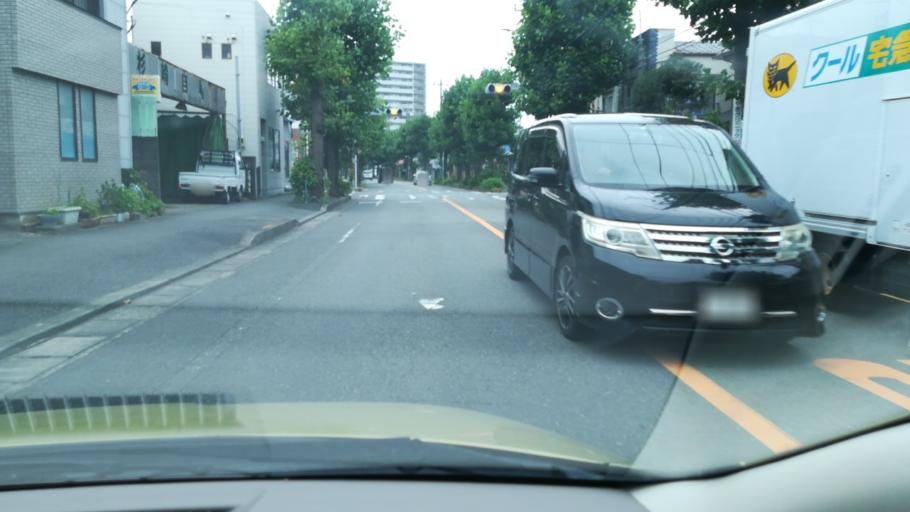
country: JP
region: Tokyo
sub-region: Machida-shi
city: Machida
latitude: 35.5706
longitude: 139.3878
